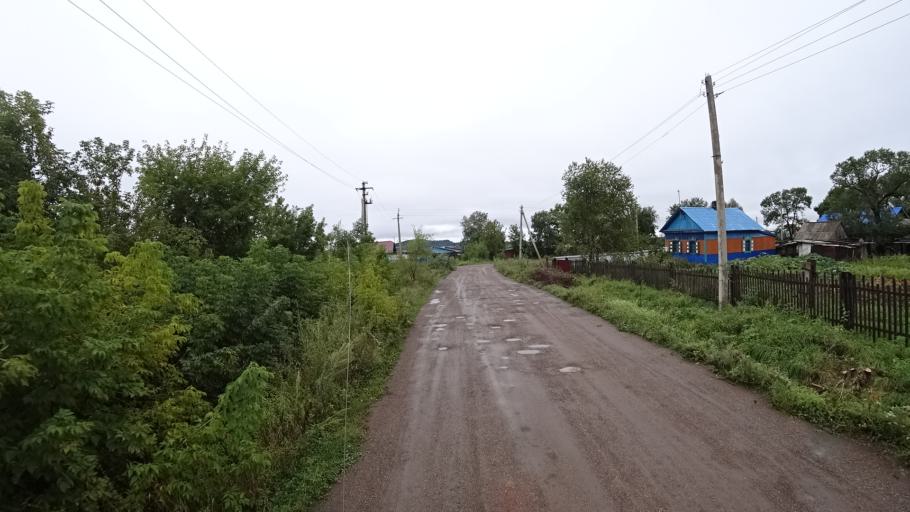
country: RU
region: Primorskiy
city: Monastyrishche
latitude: 44.1968
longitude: 132.4613
